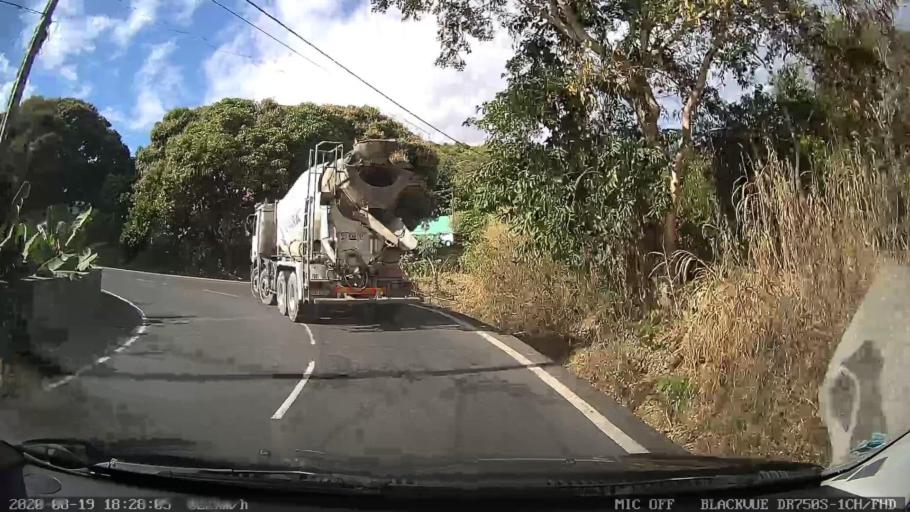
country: RE
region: Reunion
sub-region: Reunion
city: La Possession
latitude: -20.9568
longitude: 55.3516
